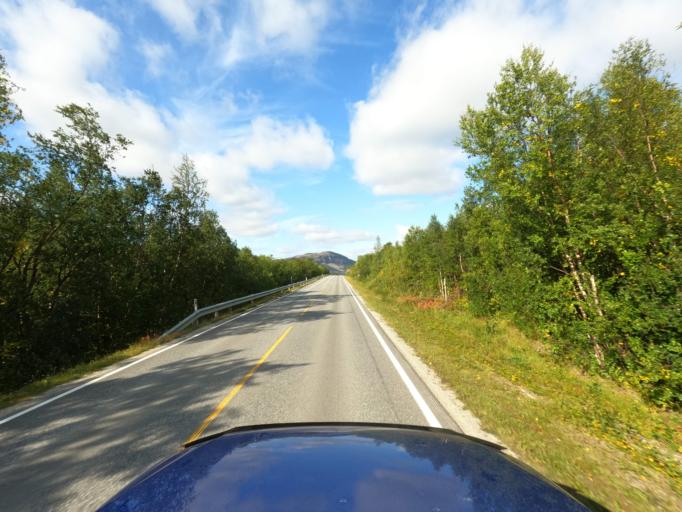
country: NO
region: Finnmark Fylke
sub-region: Porsanger
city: Lakselv
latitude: 69.9397
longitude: 24.9693
